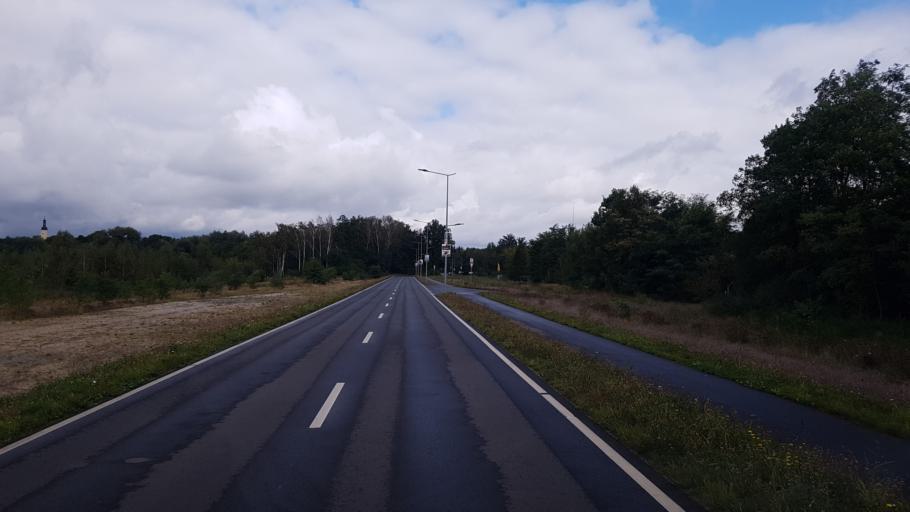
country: DE
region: Brandenburg
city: Lauchhammer
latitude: 51.4867
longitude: 13.7651
